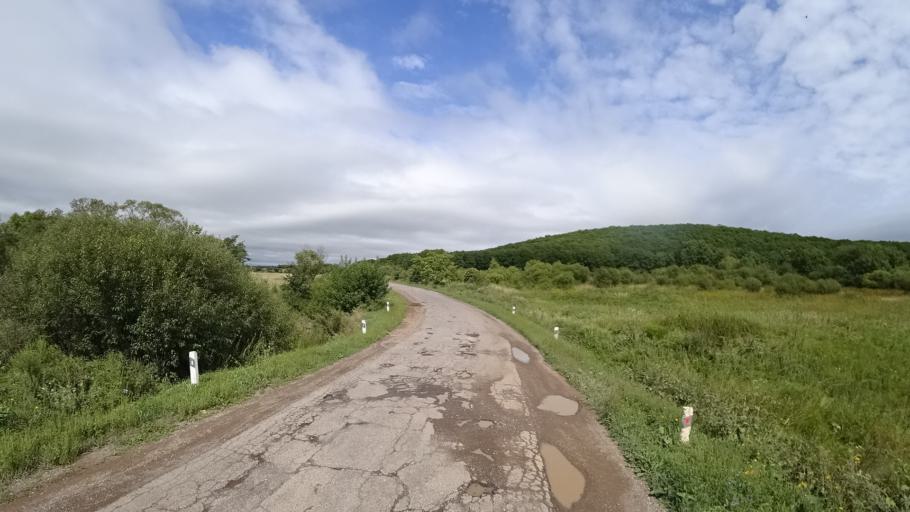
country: RU
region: Primorskiy
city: Lyalichi
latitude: 44.1492
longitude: 132.3908
